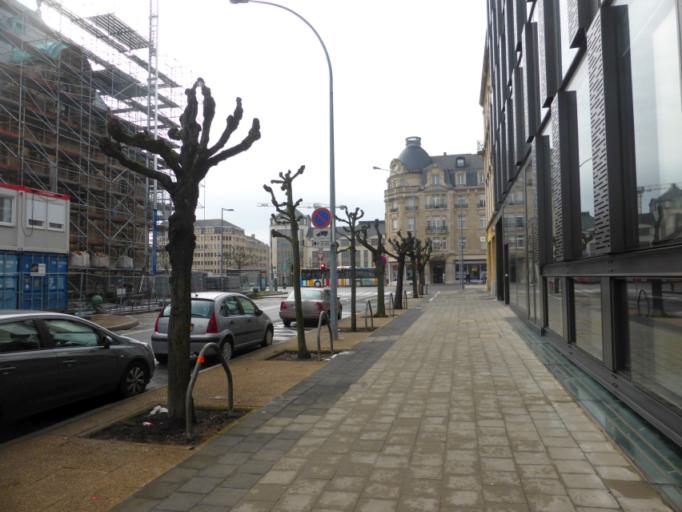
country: LU
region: Luxembourg
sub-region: Canton de Luxembourg
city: Luxembourg
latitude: 49.6055
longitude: 6.1312
